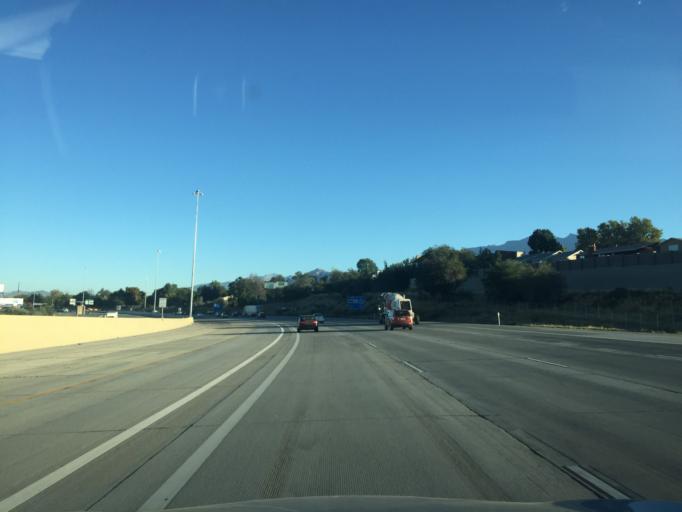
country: US
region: Utah
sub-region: Utah County
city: Provo
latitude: 40.2498
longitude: -111.6952
